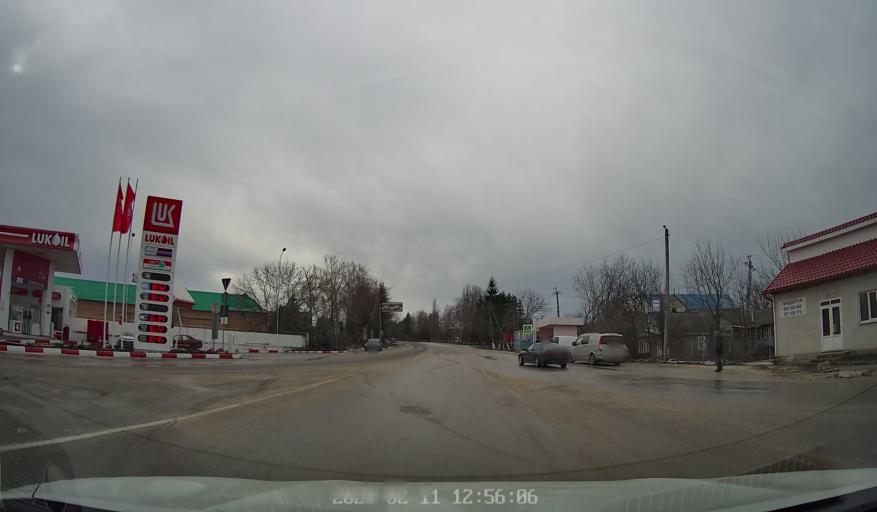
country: MD
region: Briceni
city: Briceni
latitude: 48.3507
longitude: 27.0840
